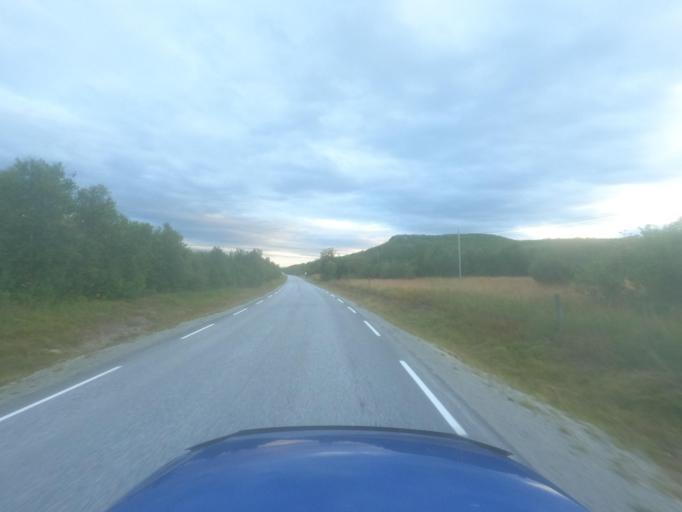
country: NO
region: Finnmark Fylke
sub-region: Porsanger
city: Lakselv
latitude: 70.2053
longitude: 24.9115
